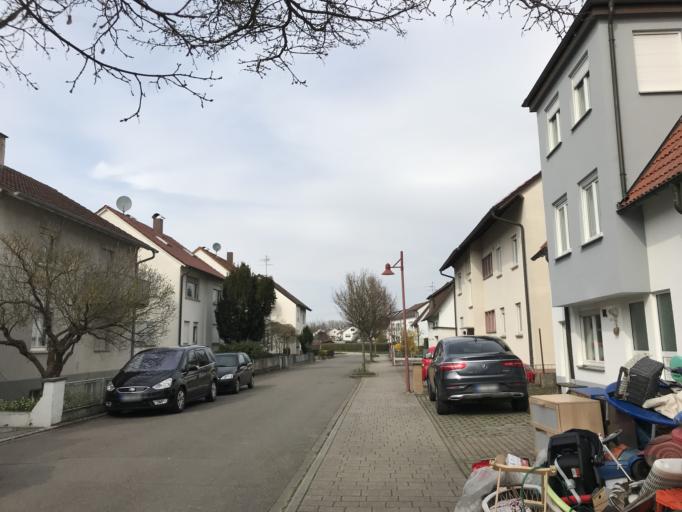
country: DE
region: Baden-Wuerttemberg
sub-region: Regierungsbezirk Stuttgart
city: Unterensingen
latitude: 48.6593
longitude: 9.3596
